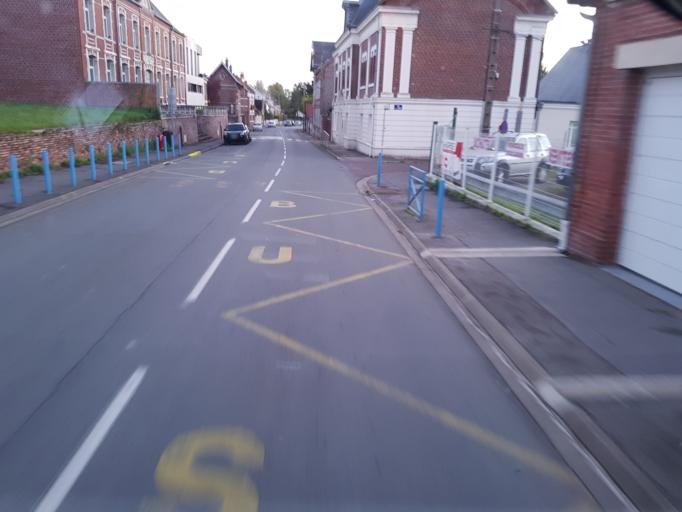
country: FR
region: Picardie
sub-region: Departement de la Somme
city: Ailly-sur-Noye
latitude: 49.7552
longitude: 2.3612
